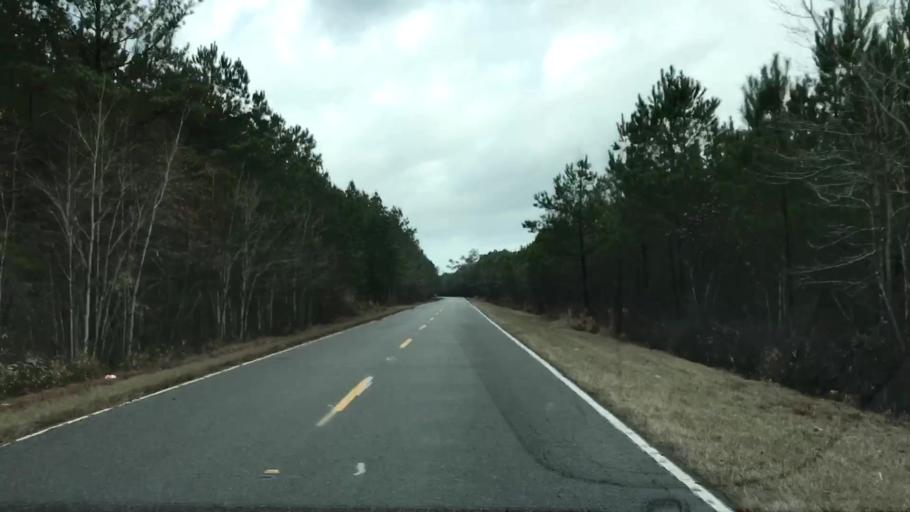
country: US
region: South Carolina
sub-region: Georgetown County
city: Murrells Inlet
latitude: 33.6298
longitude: -79.2470
